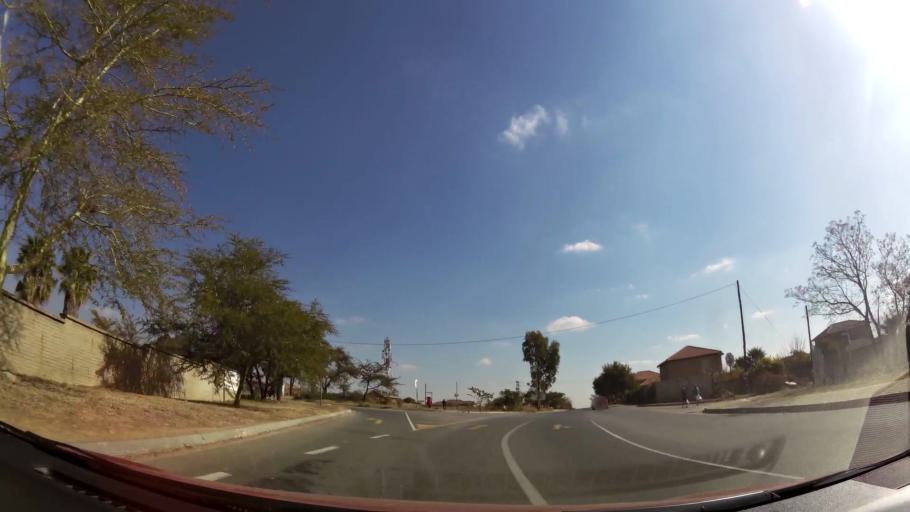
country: ZA
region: Gauteng
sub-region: West Rand District Municipality
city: Muldersdriseloop
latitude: -26.0226
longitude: 27.9405
